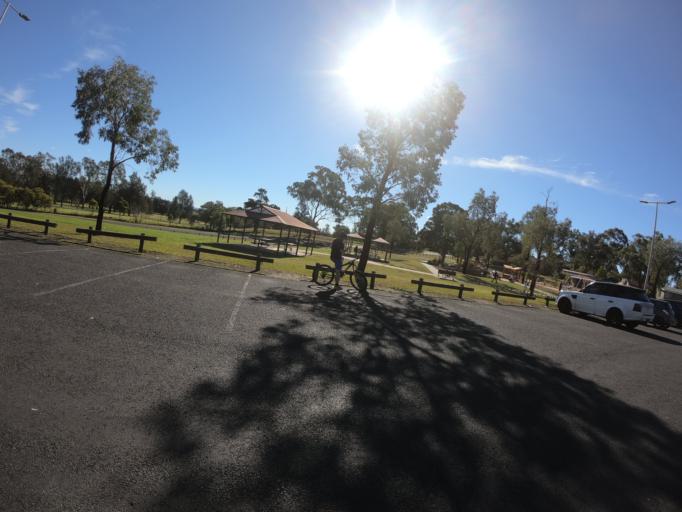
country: AU
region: New South Wales
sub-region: Hawkesbury
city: South Windsor
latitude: -33.6211
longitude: 150.8007
